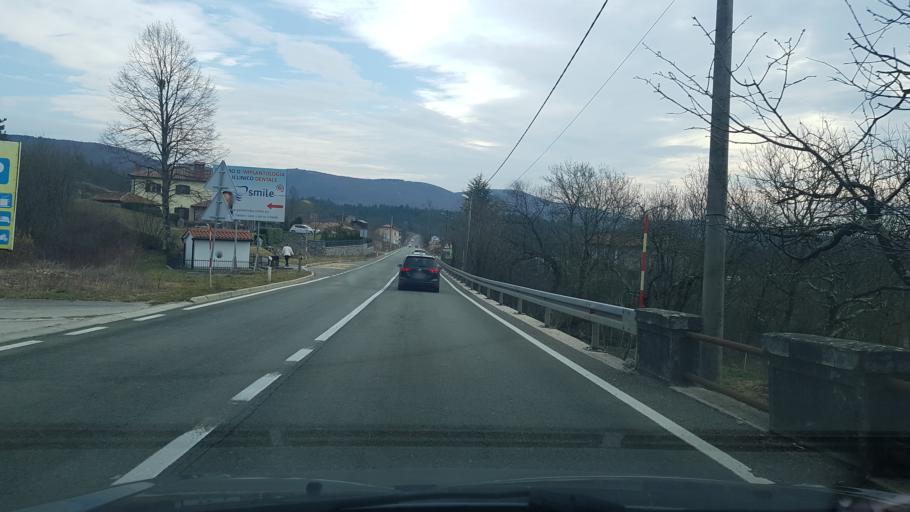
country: SI
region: Ilirska Bistrica
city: Ilirska Bistrica
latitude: 45.4805
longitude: 14.2542
